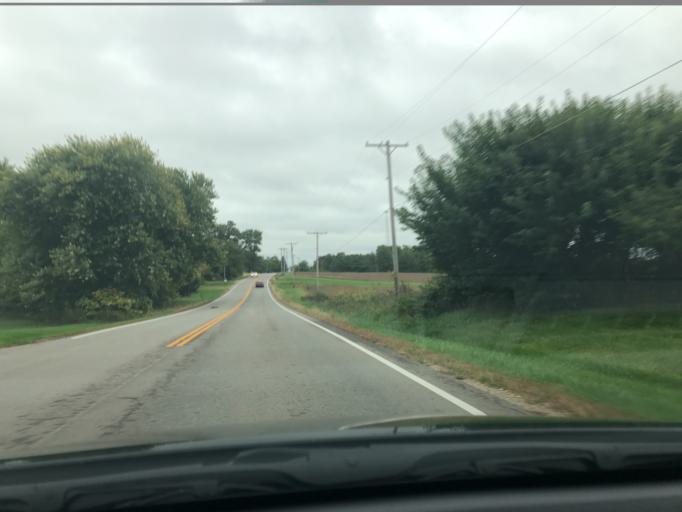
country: US
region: Ohio
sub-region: Union County
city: Marysville
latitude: 40.2605
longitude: -83.2645
